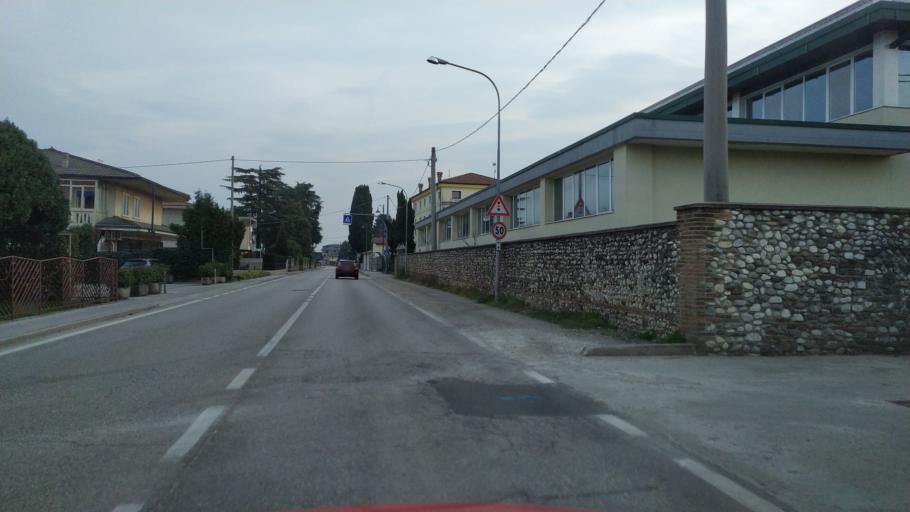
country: IT
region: Veneto
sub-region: Provincia di Vicenza
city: Montecchio Precalcino
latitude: 45.6683
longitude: 11.5630
